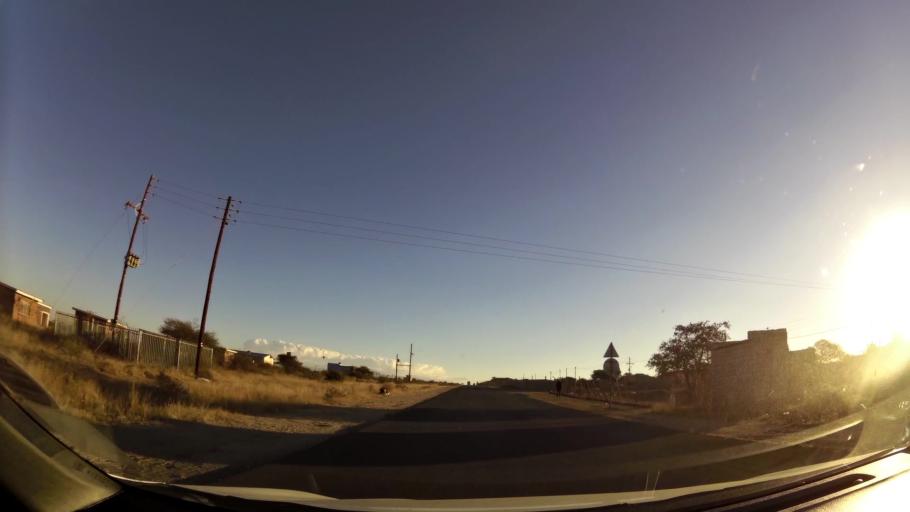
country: ZA
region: Limpopo
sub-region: Capricorn District Municipality
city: Polokwane
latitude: -23.8306
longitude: 29.3736
